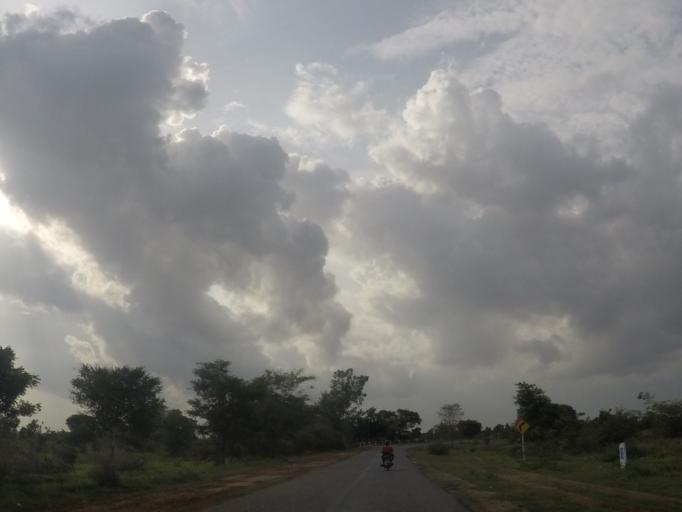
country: MM
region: Mandalay
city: Meiktila
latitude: 20.5313
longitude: 95.6917
